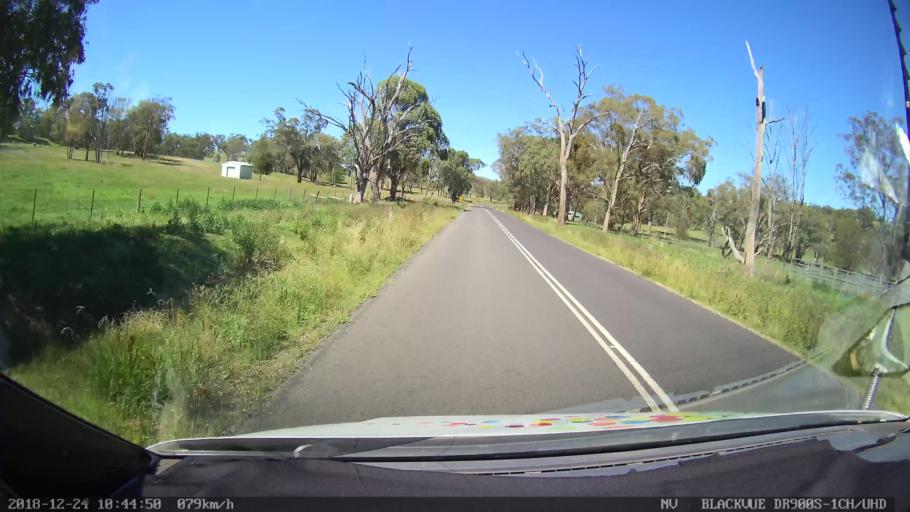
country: AU
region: New South Wales
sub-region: Upper Hunter Shire
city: Merriwa
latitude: -31.8969
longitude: 150.4409
